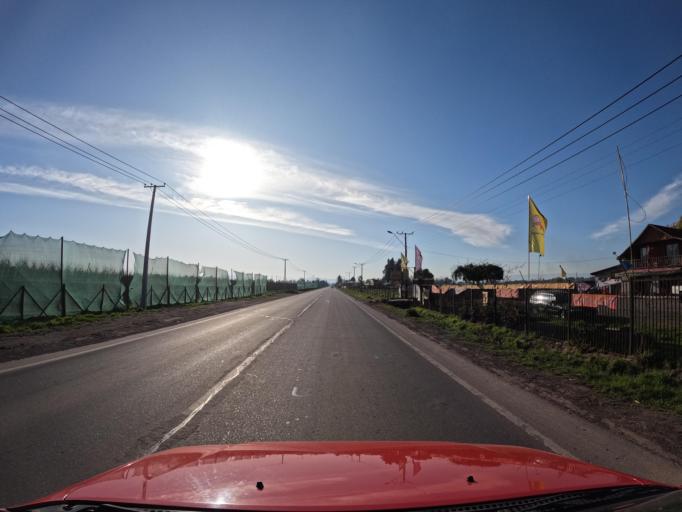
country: CL
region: Maule
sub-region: Provincia de Curico
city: Teno
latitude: -34.8947
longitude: -71.0634
